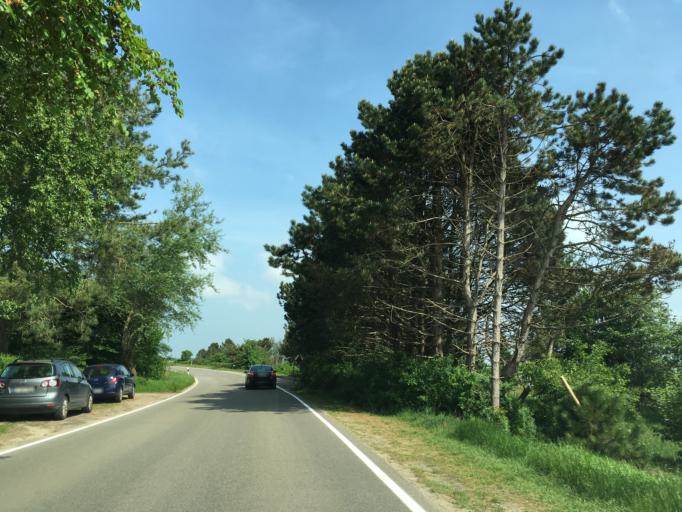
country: DE
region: Schleswig-Holstein
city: Nebel
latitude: 54.6522
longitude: 8.3459
